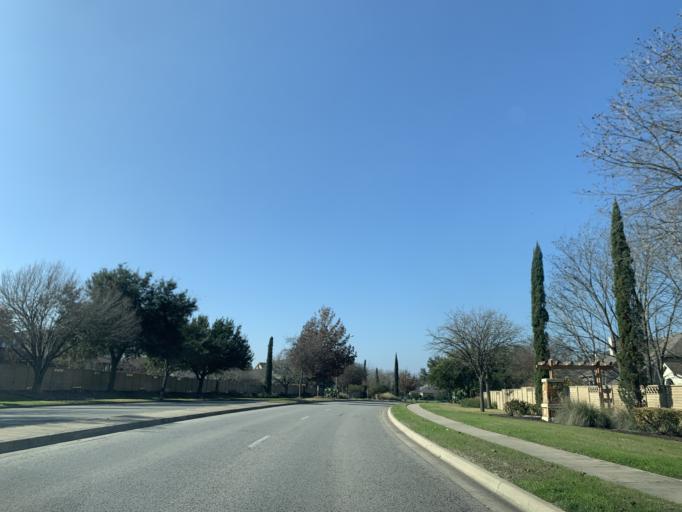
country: US
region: Texas
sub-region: Williamson County
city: Round Rock
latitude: 30.5074
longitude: -97.6253
